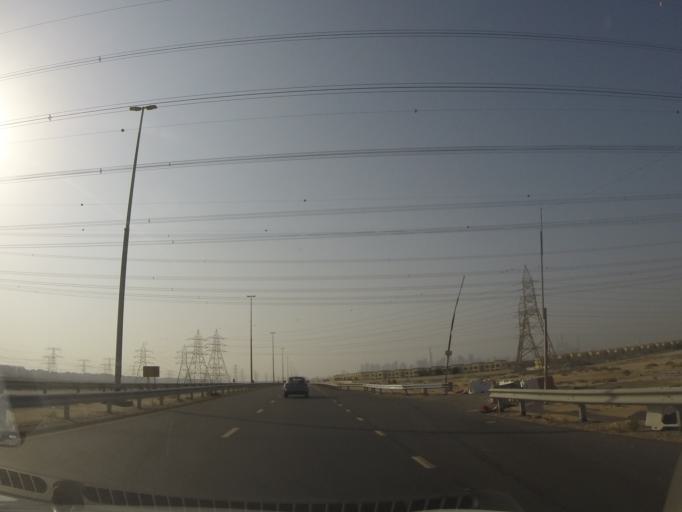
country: AE
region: Dubai
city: Dubai
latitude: 25.0362
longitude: 55.1619
